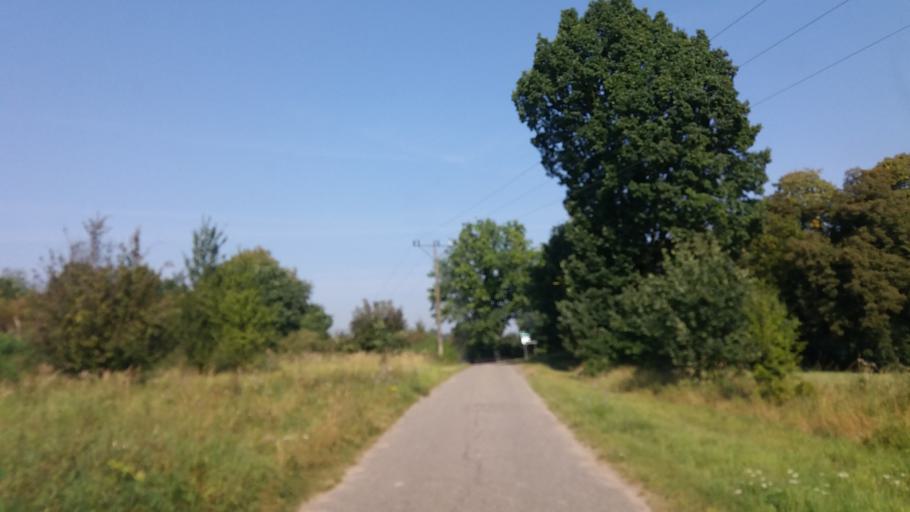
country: PL
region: West Pomeranian Voivodeship
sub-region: Powiat choszczenski
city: Pelczyce
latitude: 52.9780
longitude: 15.3374
